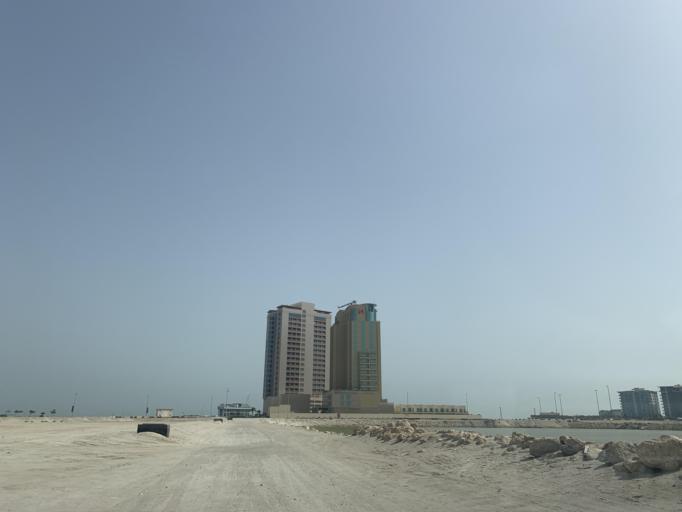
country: BH
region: Manama
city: Jidd Hafs
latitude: 26.2386
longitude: 50.5572
